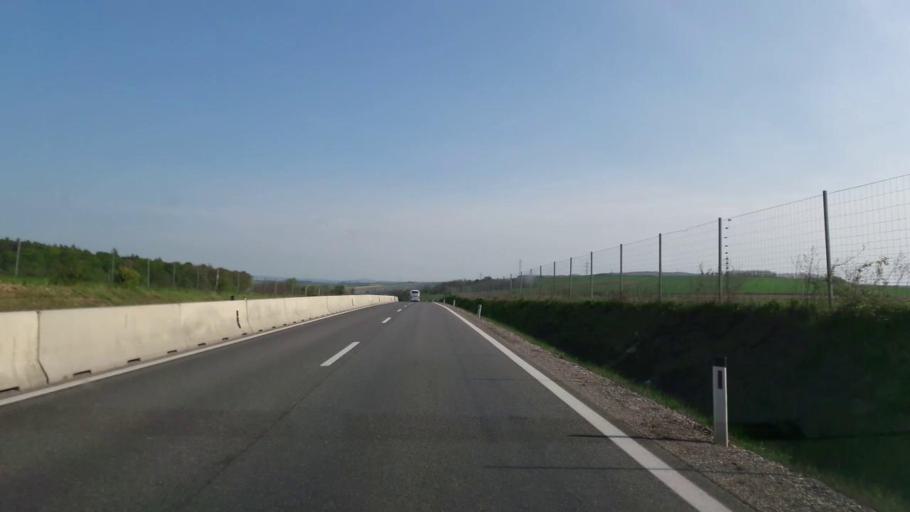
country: AT
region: Lower Austria
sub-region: Politischer Bezirk Hollabrunn
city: Hollabrunn
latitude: 48.5307
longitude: 16.0814
